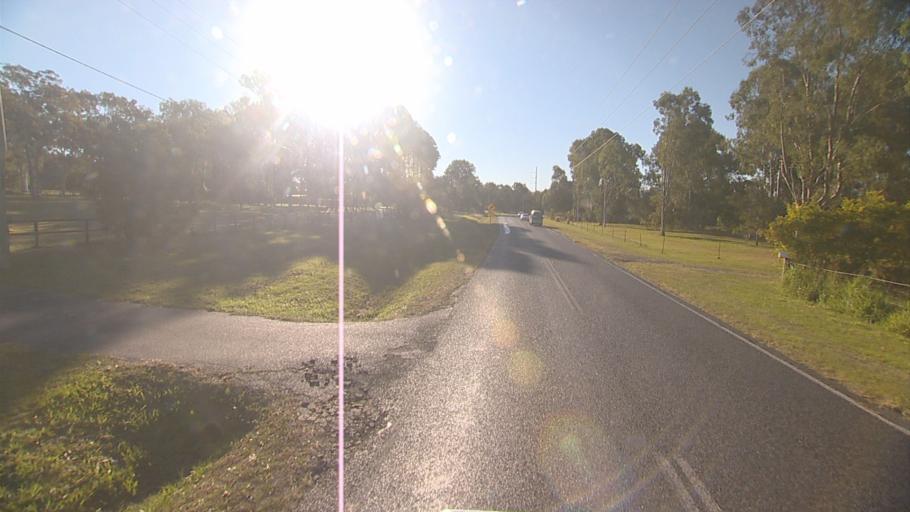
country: AU
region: Queensland
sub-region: Logan
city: Chambers Flat
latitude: -27.7452
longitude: 153.0890
